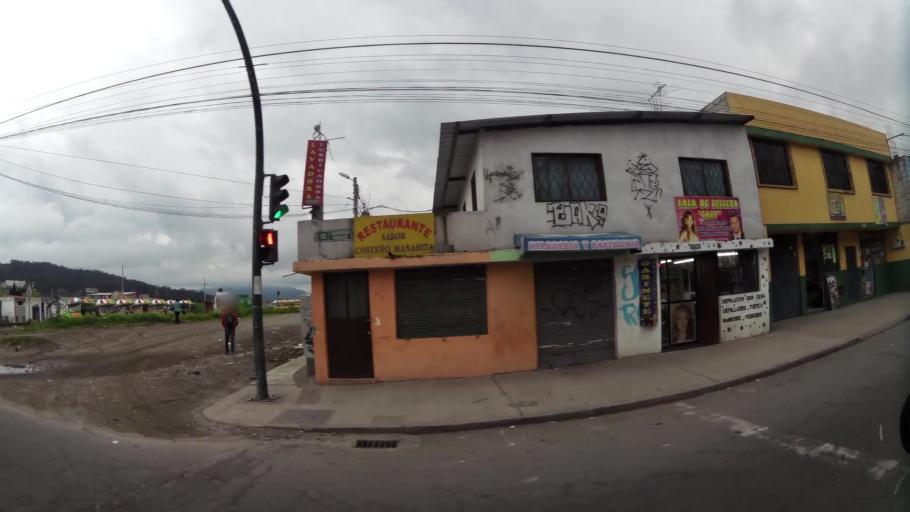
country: EC
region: Pichincha
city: Sangolqui
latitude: -0.3281
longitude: -78.5388
